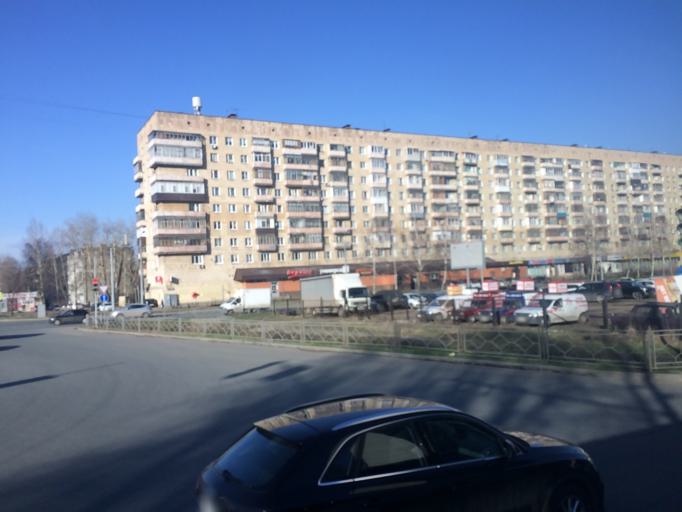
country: RU
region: Tatarstan
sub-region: Gorod Kazan'
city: Kazan
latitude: 55.8213
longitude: 49.0496
